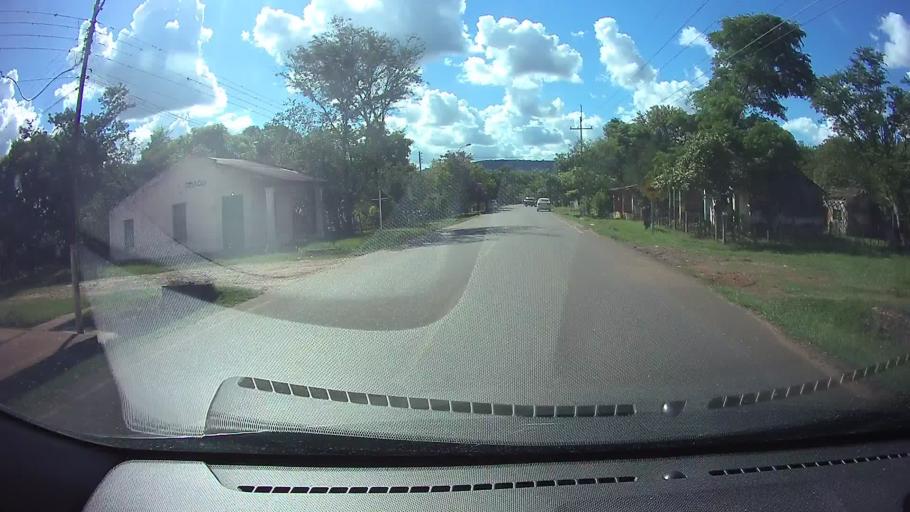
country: PY
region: Paraguari
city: Sapucai
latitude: -25.6872
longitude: -56.8622
